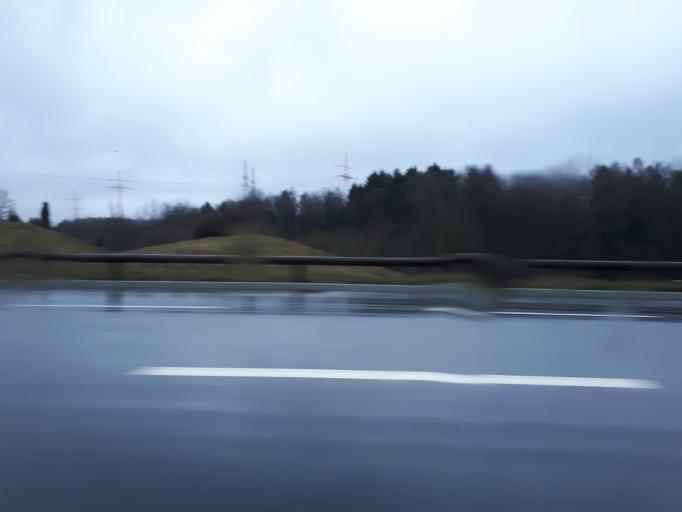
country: LU
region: Luxembourg
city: Kirchberg
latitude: 49.6345
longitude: 6.1778
